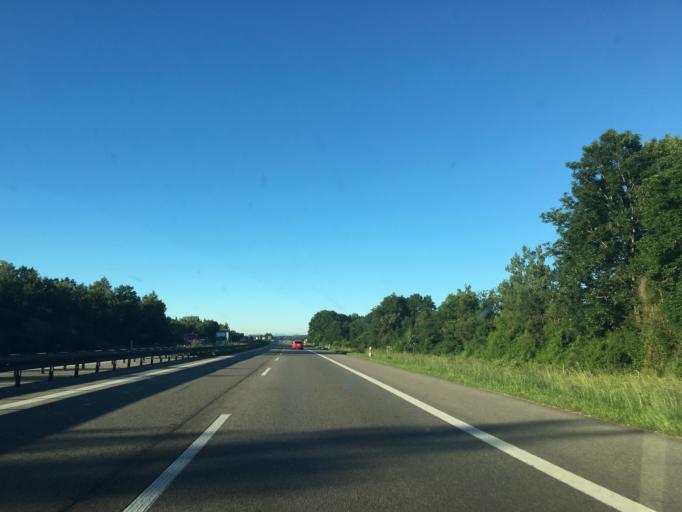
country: DE
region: Bavaria
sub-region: Swabia
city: Heimertingen
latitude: 48.0339
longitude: 10.1315
